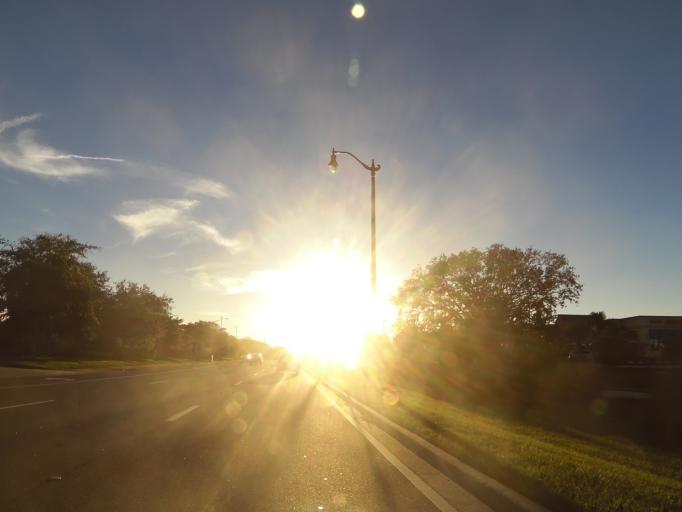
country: US
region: Florida
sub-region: Flagler County
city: Palm Coast
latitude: 29.5569
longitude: -81.2075
